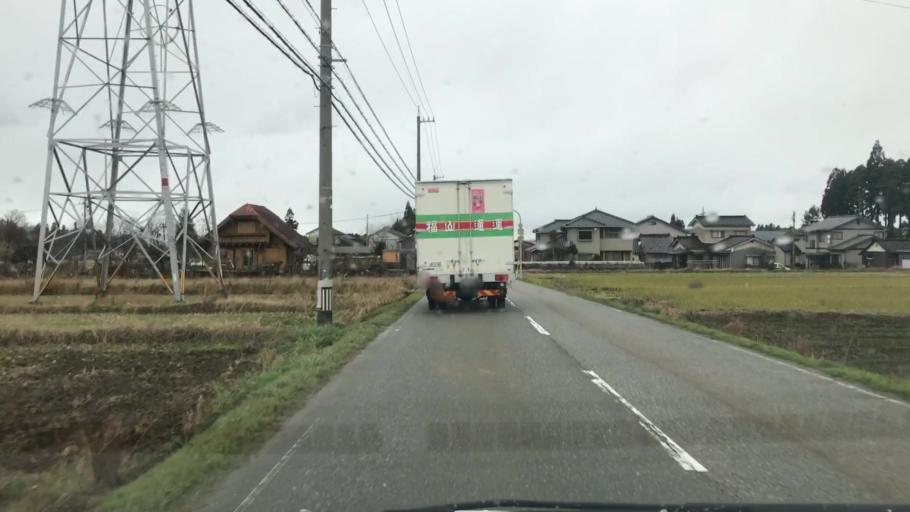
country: JP
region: Toyama
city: Kamiichi
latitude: 36.5991
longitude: 137.3232
